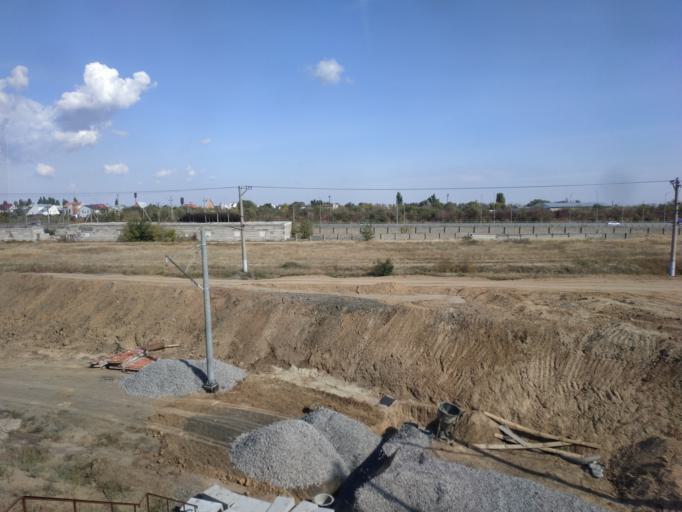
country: RU
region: Volgograd
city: Gumrak
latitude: 48.7708
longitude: 44.3907
